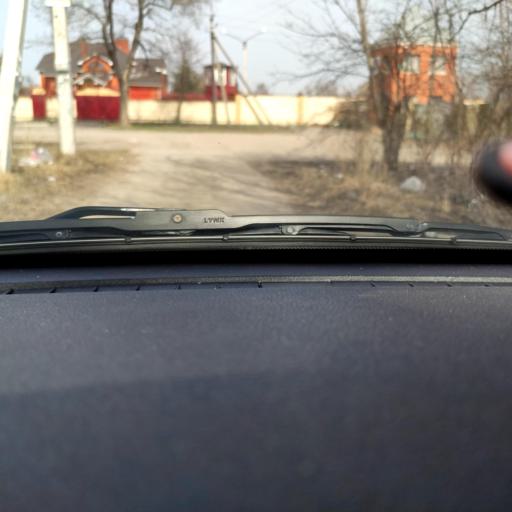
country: RU
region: Voronezj
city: Novaya Usman'
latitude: 51.6264
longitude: 39.4156
